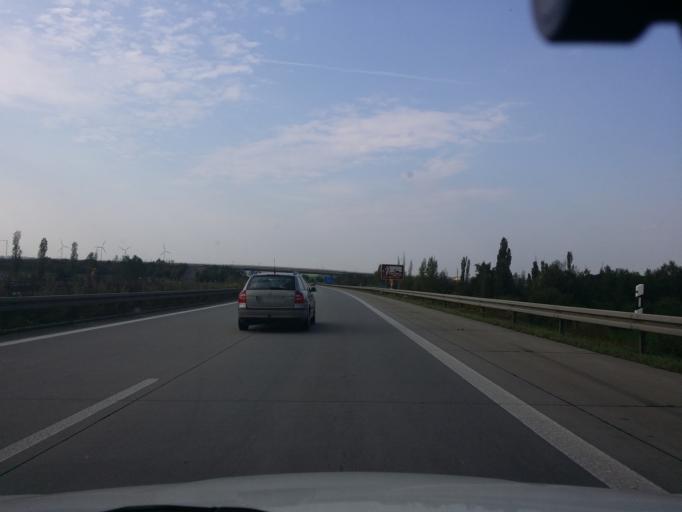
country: DE
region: Saxony
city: Zwenkau
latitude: 51.2588
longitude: 12.2917
